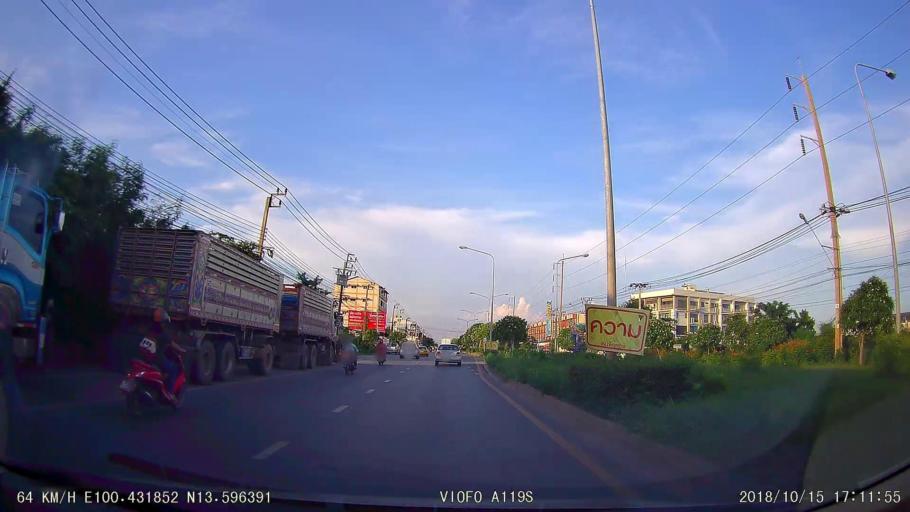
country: TH
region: Bangkok
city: Bang Khun Thian
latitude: 13.5967
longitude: 100.4319
